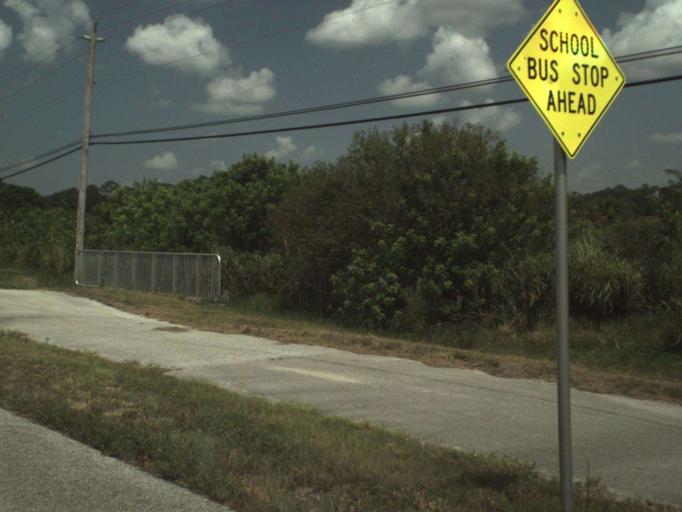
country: US
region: Florida
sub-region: Saint Lucie County
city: Fort Pierce South
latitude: 27.4113
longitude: -80.4101
